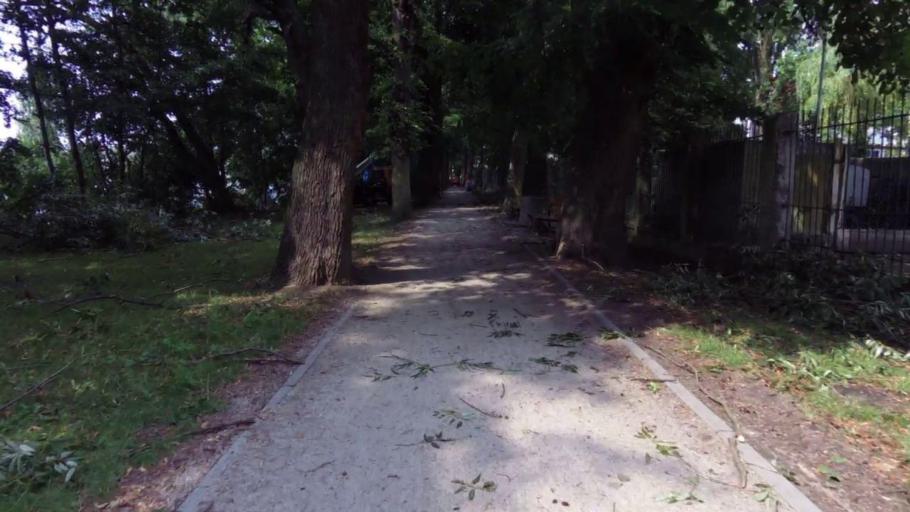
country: PL
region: West Pomeranian Voivodeship
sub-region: Powiat choszczenski
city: Choszczno
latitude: 53.1643
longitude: 15.4129
